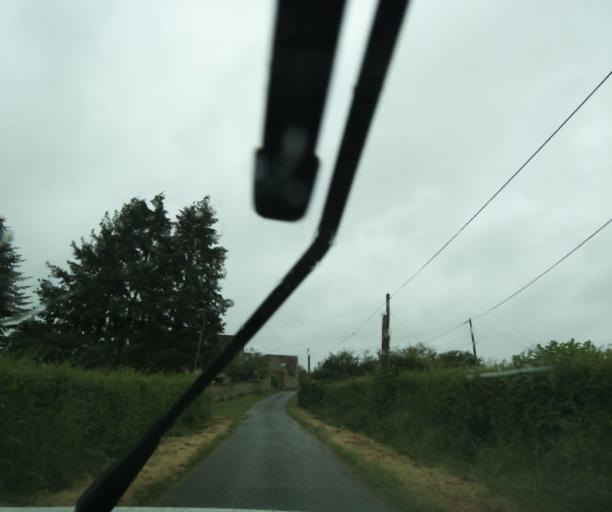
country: FR
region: Bourgogne
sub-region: Departement de Saone-et-Loire
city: Palinges
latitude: 46.5472
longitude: 4.2122
